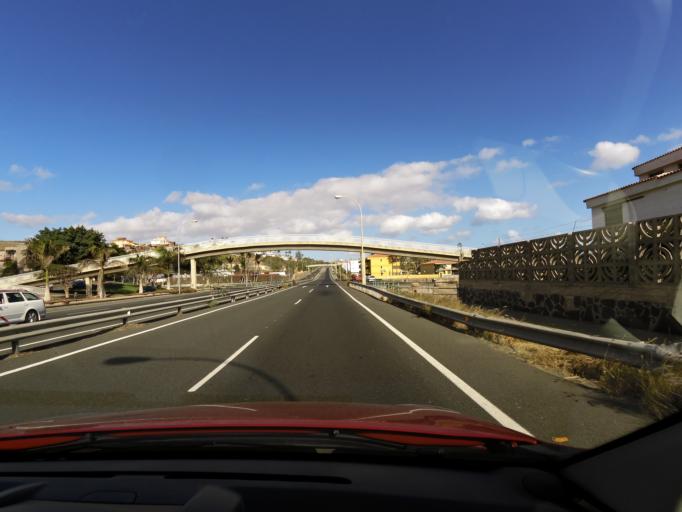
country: ES
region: Canary Islands
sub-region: Provincia de Las Palmas
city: Playa del Ingles
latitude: 27.7664
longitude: -15.5547
